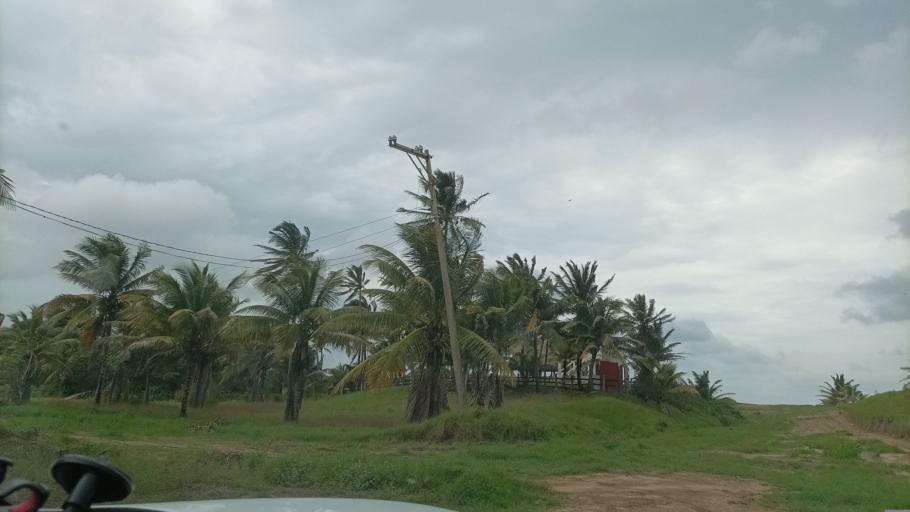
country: MX
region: Veracruz
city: Agua Dulce
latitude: 18.2078
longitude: -94.1479
